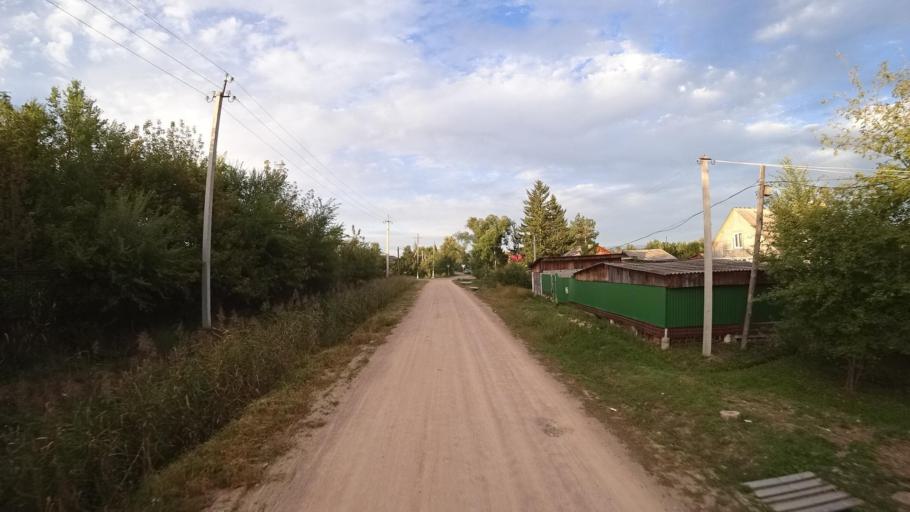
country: RU
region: Primorskiy
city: Yakovlevka
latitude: 44.4258
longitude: 133.4814
